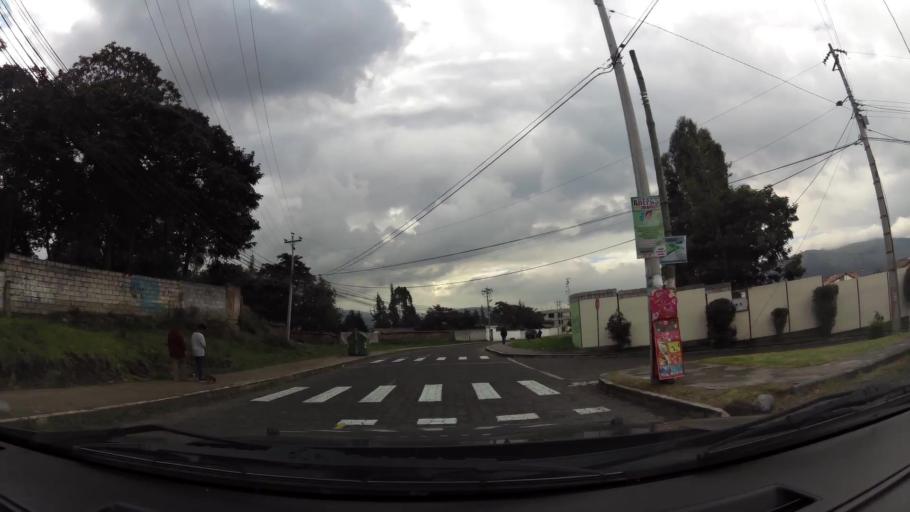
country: EC
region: Pichincha
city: Sangolqui
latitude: -0.3228
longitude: -78.4563
